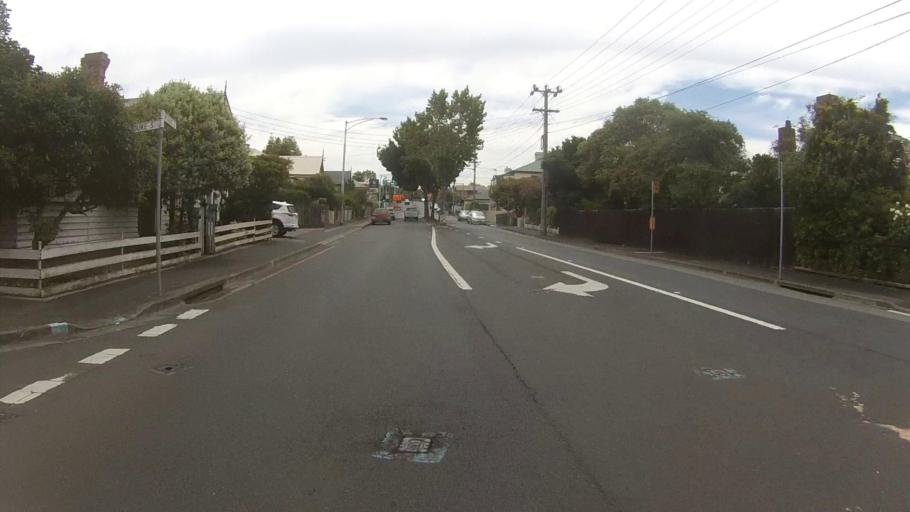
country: AU
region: Tasmania
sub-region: Hobart
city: Sandy Bay
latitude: -42.8983
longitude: 147.3240
